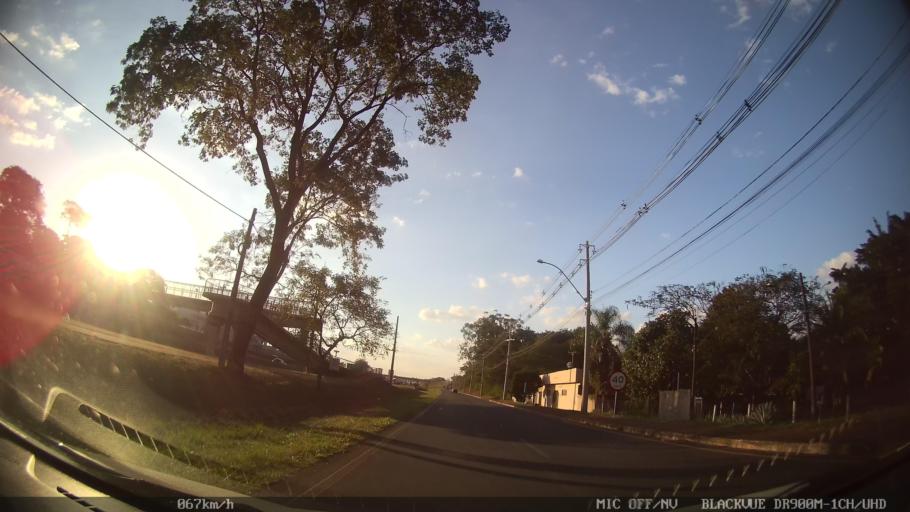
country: BR
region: Sao Paulo
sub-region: Ribeirao Preto
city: Ribeirao Preto
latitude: -21.1545
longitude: -47.7566
